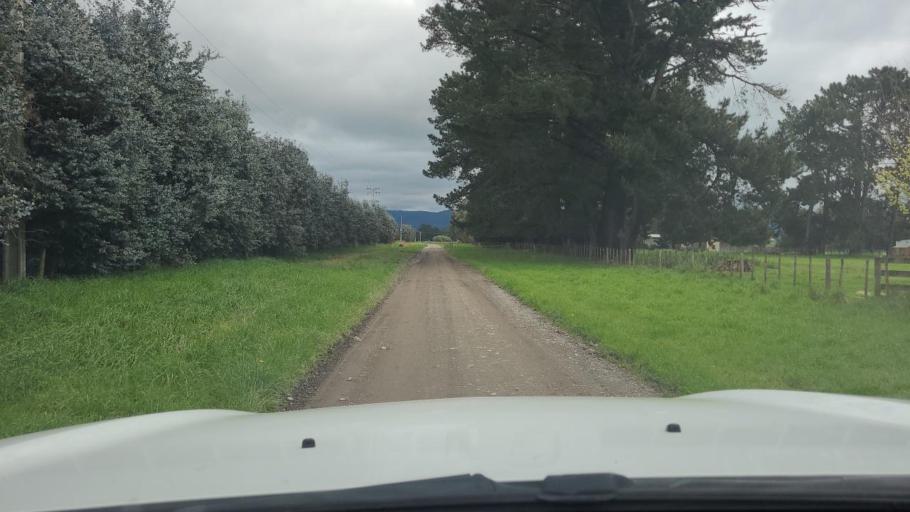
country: NZ
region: Wellington
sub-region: Masterton District
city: Masterton
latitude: -41.1276
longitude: 175.4254
